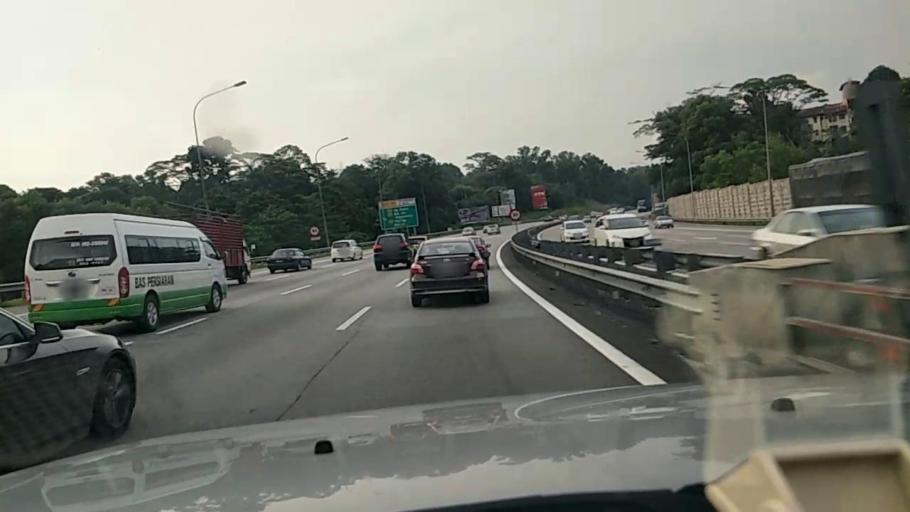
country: MY
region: Selangor
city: Kampung Baru Subang
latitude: 3.1913
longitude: 101.5831
